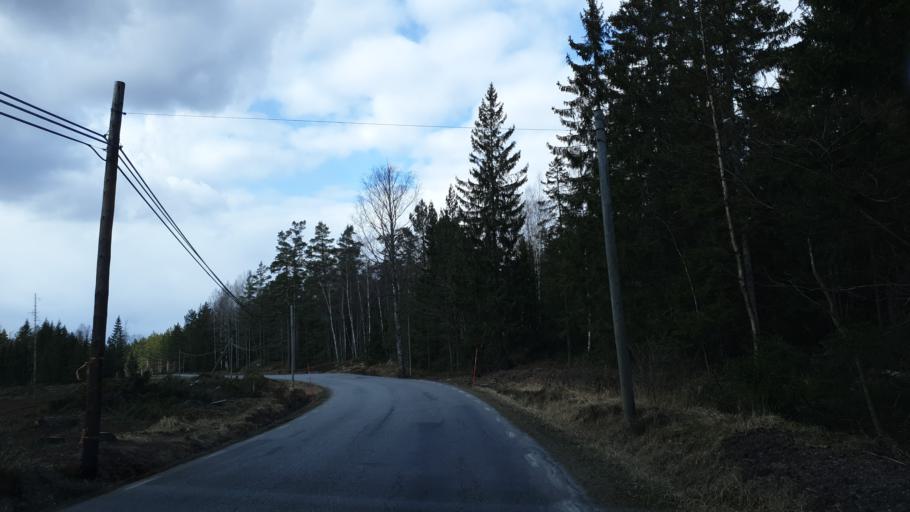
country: SE
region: Stockholm
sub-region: Tyreso Kommun
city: Brevik
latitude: 59.2489
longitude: 18.4409
